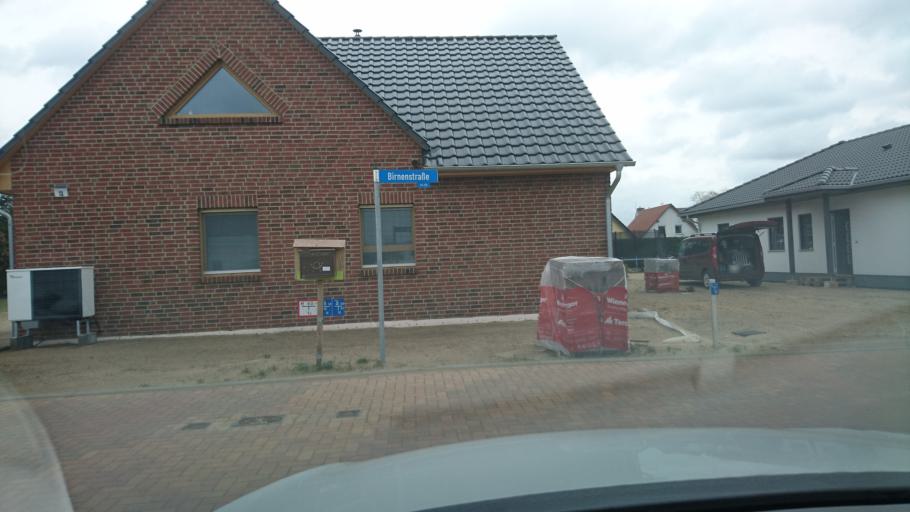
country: DE
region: Brandenburg
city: Gross Kreutz
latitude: 52.4031
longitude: 12.7910
